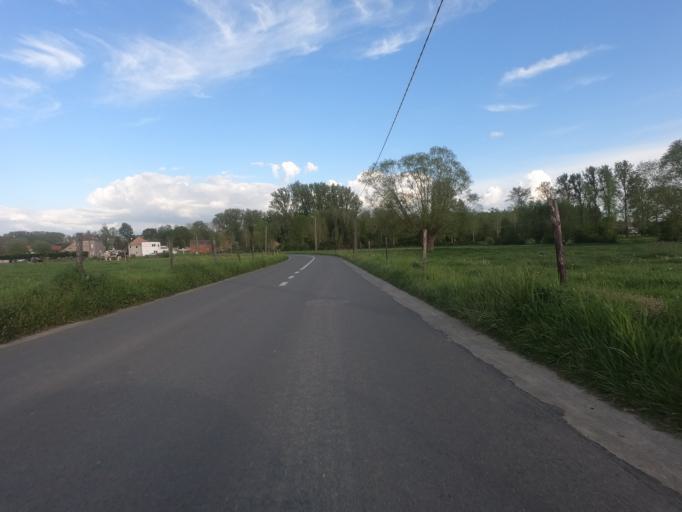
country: BE
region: Flanders
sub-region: Provincie Vlaams-Brabant
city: Galmaarden
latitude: 50.7527
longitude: 3.9915
